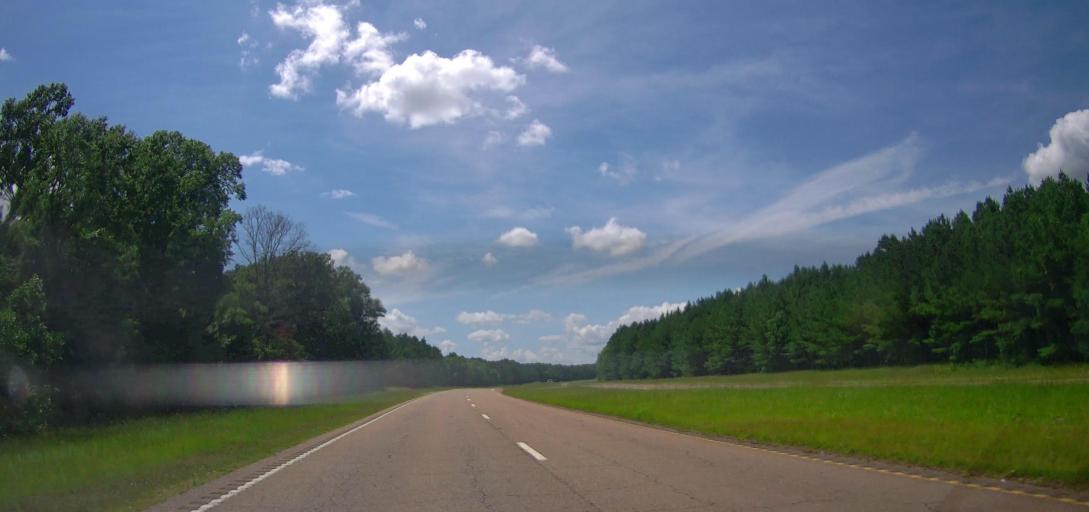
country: US
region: Mississippi
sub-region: Monroe County
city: Aberdeen
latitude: 33.8154
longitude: -88.5745
